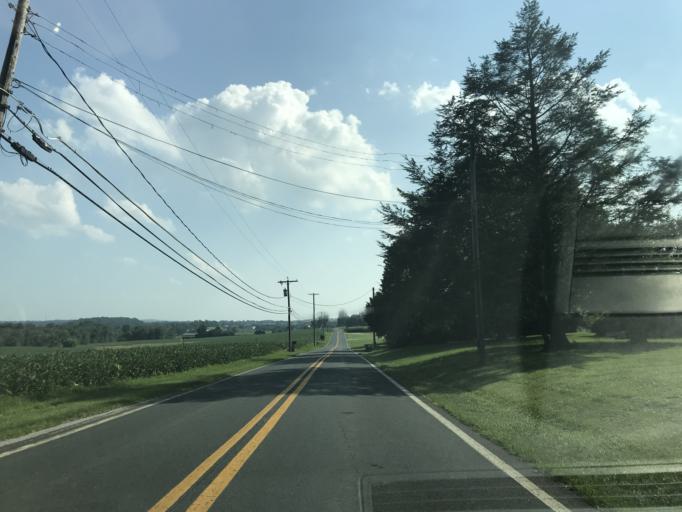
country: US
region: Maryland
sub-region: Carroll County
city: Westminster
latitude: 39.6193
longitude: -76.9780
